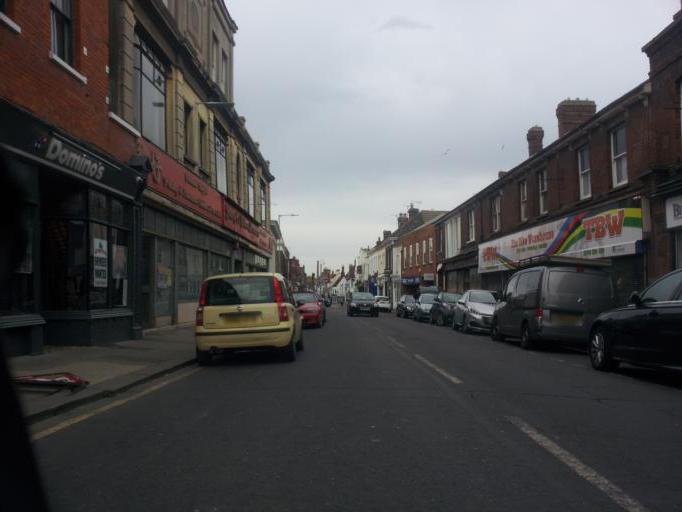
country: GB
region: England
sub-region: Kent
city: Faversham
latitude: 51.3130
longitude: 0.8906
